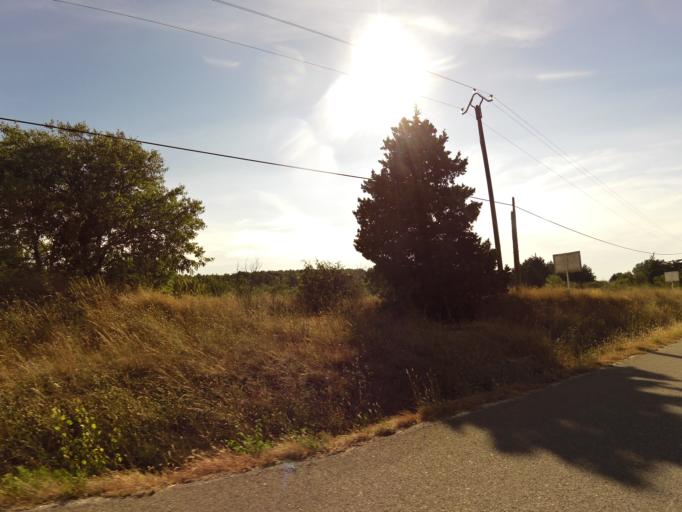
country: FR
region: Languedoc-Roussillon
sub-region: Departement du Gard
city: Milhaud
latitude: 43.8158
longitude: 4.3035
